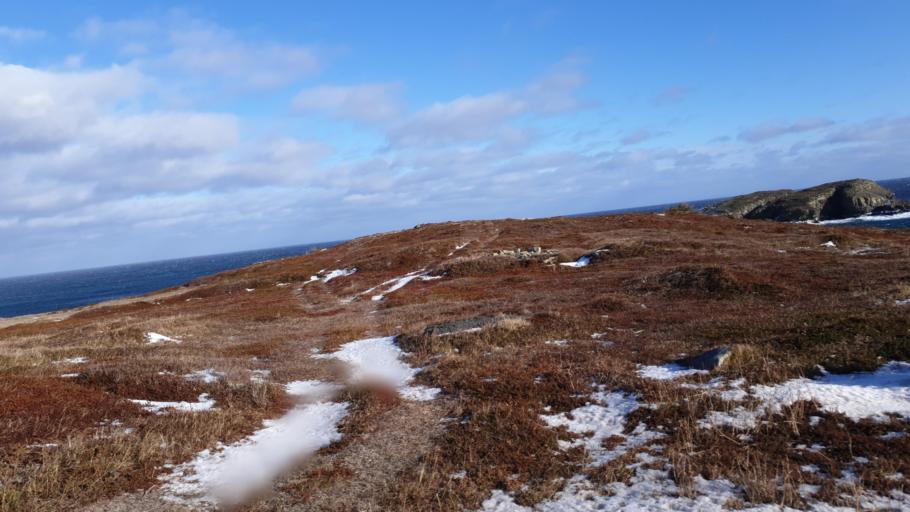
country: CA
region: Newfoundland and Labrador
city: Bonavista
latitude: 48.6235
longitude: -53.0173
